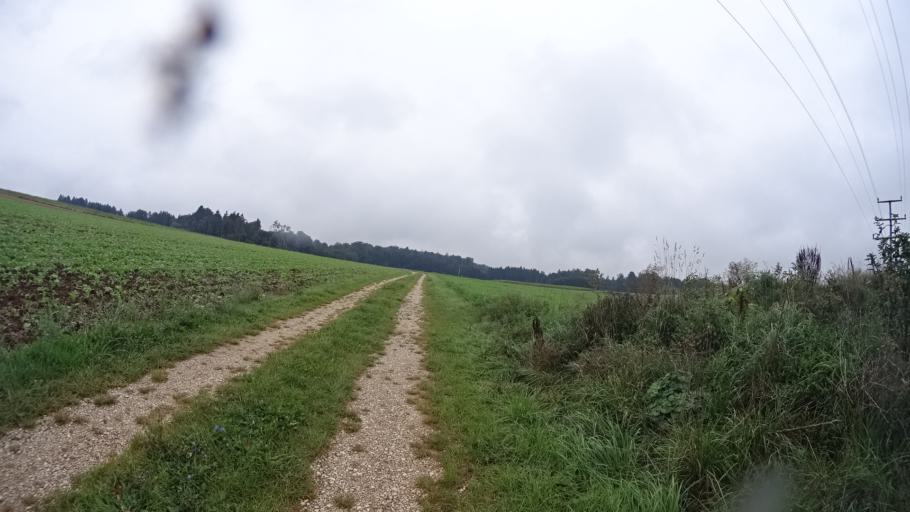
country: DE
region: Bavaria
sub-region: Upper Bavaria
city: Bohmfeld
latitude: 48.9103
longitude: 11.3814
